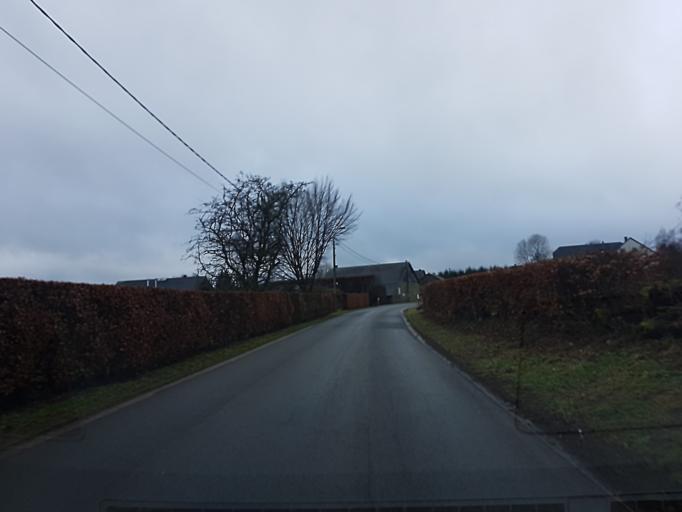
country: BE
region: Wallonia
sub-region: Province de Liege
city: Malmedy
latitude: 50.4640
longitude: 6.0690
